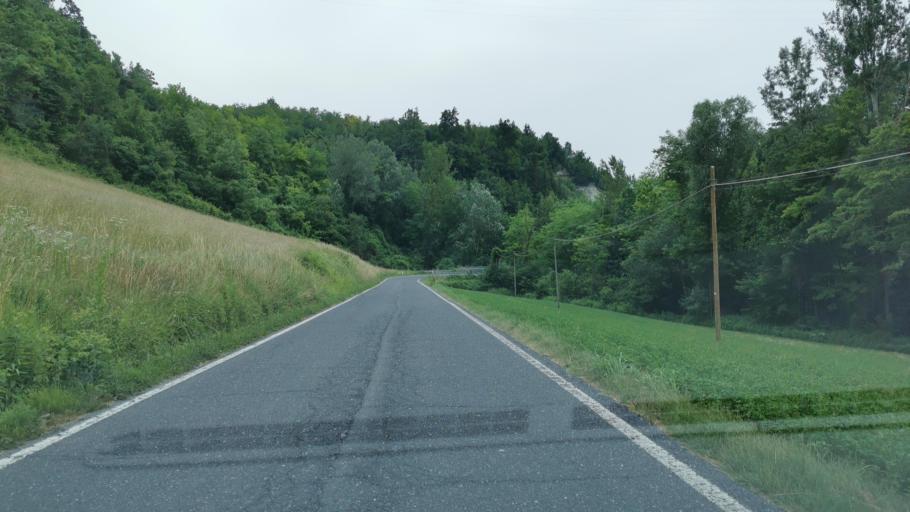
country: IT
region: Piedmont
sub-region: Provincia di Cuneo
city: Ceva
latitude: 44.3958
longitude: 8.0478
